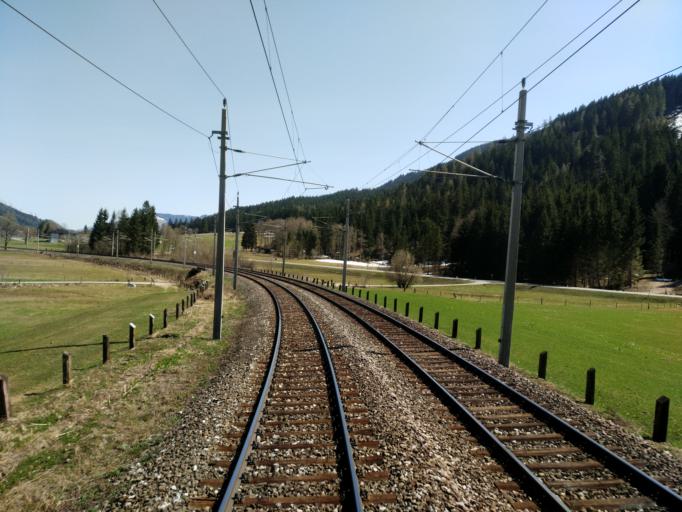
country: AT
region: Tyrol
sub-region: Politischer Bezirk Kitzbuhel
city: Hochfilzen
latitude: 47.4544
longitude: 12.6581
